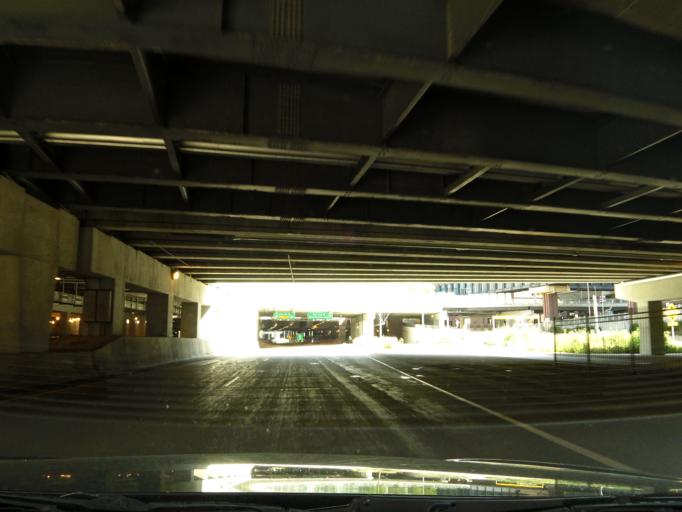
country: US
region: Minnesota
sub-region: Hennepin County
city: Minneapolis
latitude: 44.9801
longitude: -93.2779
